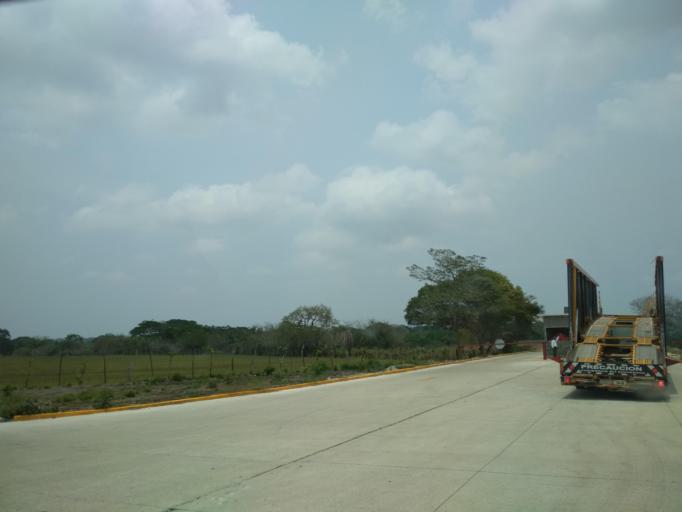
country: MX
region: Veracruz
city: Manlio Fabio Altamirano
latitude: 19.1383
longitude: -96.2989
